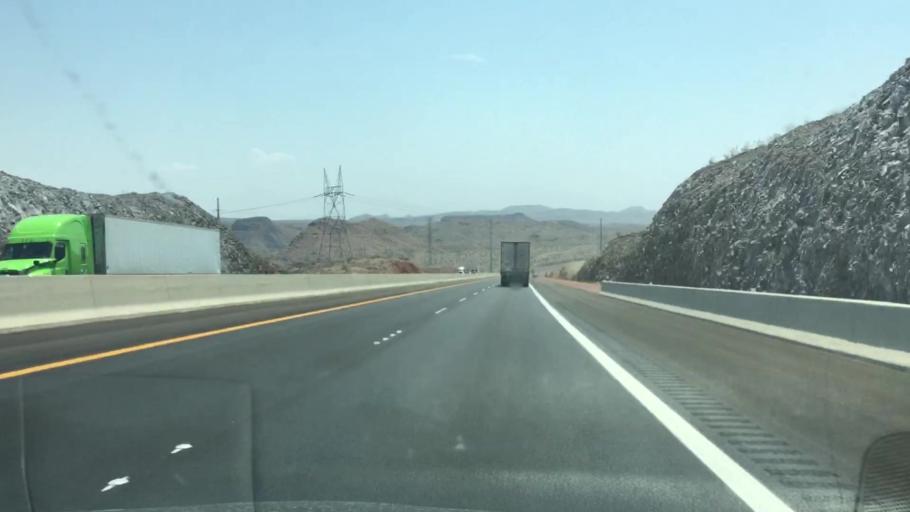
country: US
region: Nevada
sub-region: Clark County
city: Boulder City
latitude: 35.9858
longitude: -114.7959
